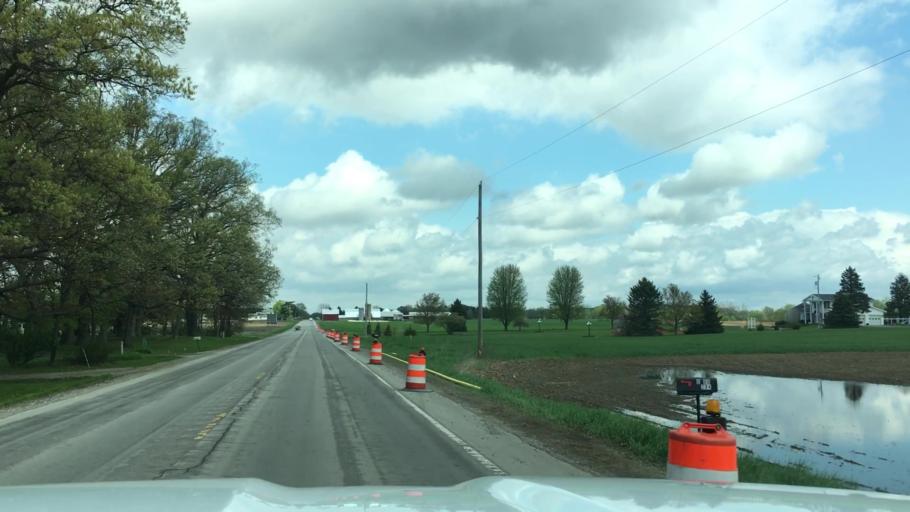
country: US
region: Michigan
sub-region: Ingham County
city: Stockbridge
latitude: 42.4599
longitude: -84.1900
